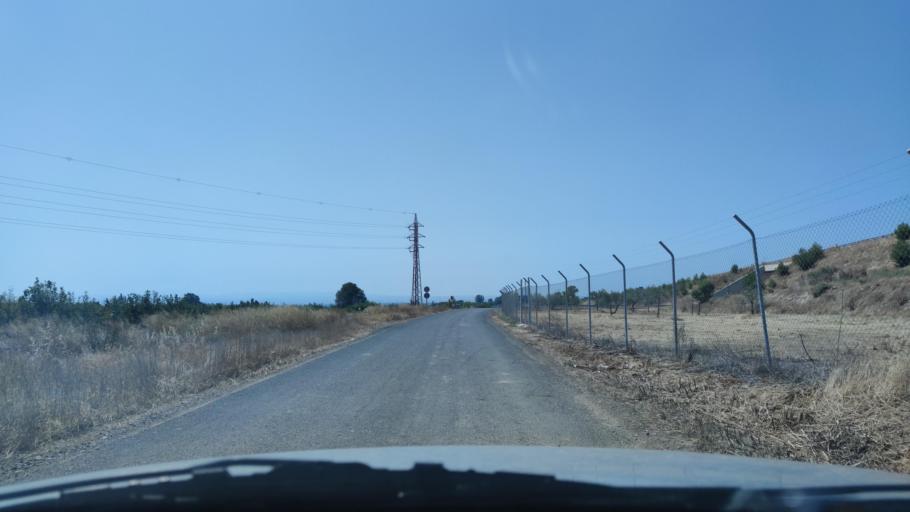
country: ES
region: Catalonia
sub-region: Provincia de Lleida
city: Alpicat
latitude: 41.6654
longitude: 0.5813
